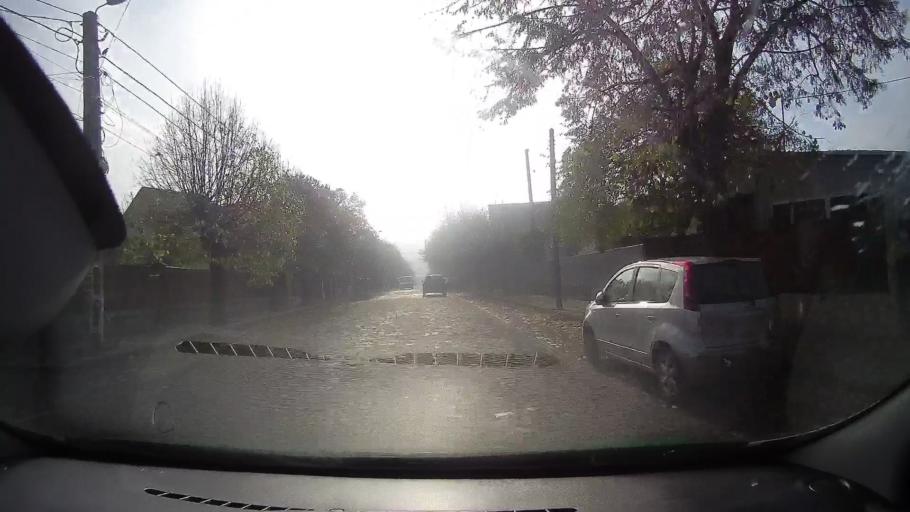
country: RO
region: Tulcea
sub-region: Municipiul Tulcea
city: Tulcea
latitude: 45.1682
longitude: 28.8144
